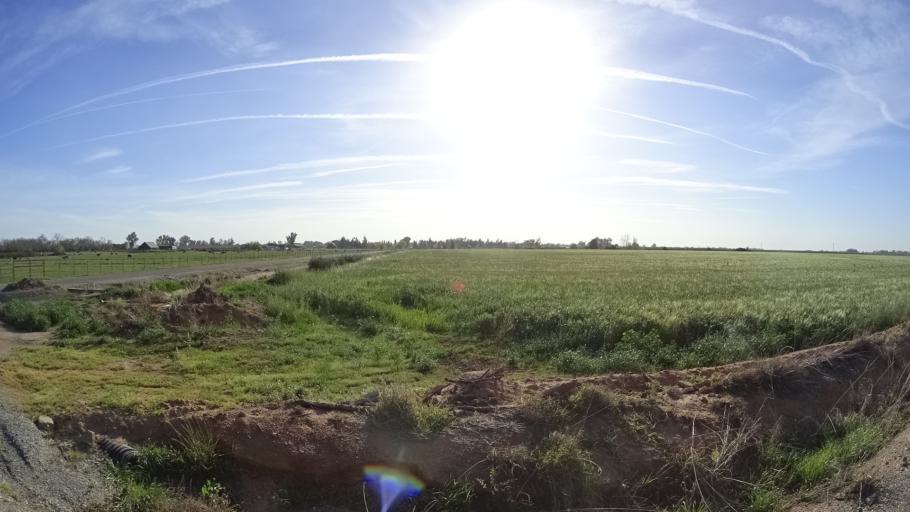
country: US
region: California
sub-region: Glenn County
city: Orland
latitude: 39.7148
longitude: -122.2351
